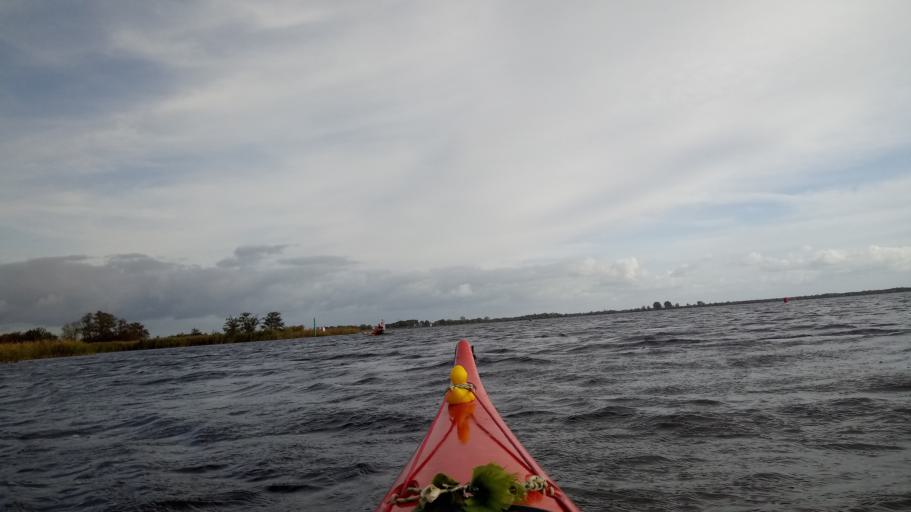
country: NL
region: Overijssel
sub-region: Gemeente Steenwijkerland
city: Sint Jansklooster
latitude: 52.6839
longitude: 6.0467
